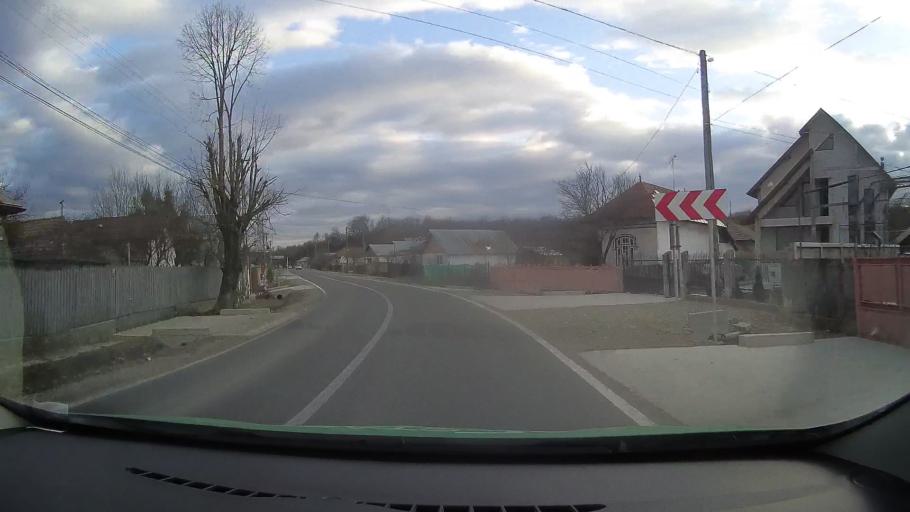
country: RO
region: Dambovita
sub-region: Comuna I. L. Caragiale
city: Mija
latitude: 44.9193
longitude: 25.6886
